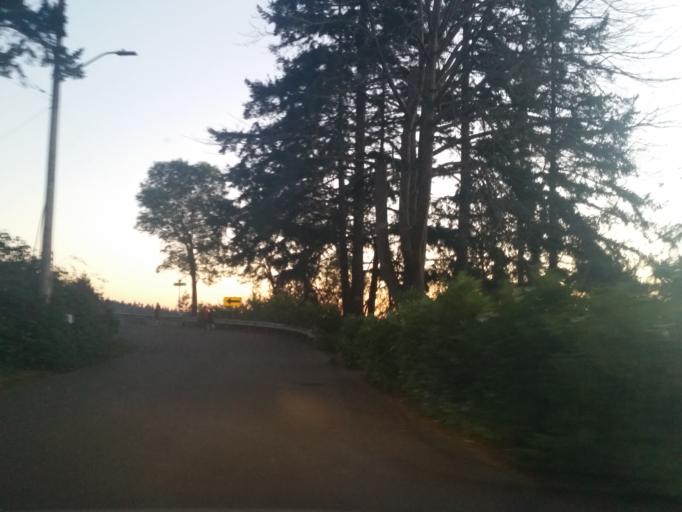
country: US
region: Washington
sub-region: Snohomish County
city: Woodway
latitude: 47.7675
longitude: -122.3853
